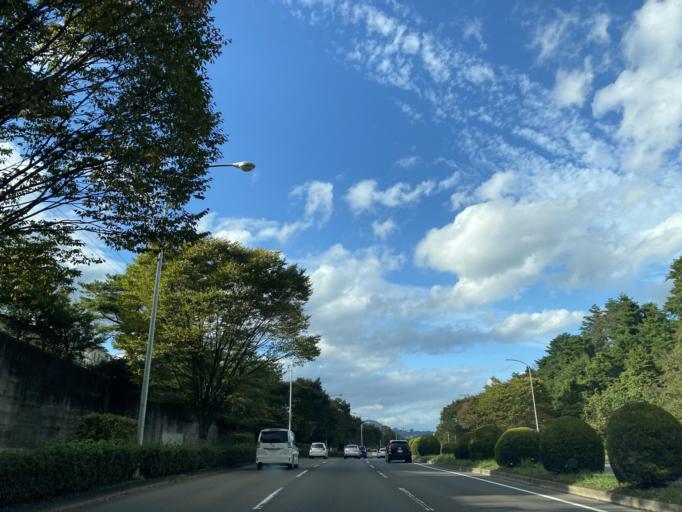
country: JP
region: Miyagi
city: Sendai-shi
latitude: 38.3136
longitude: 140.8451
